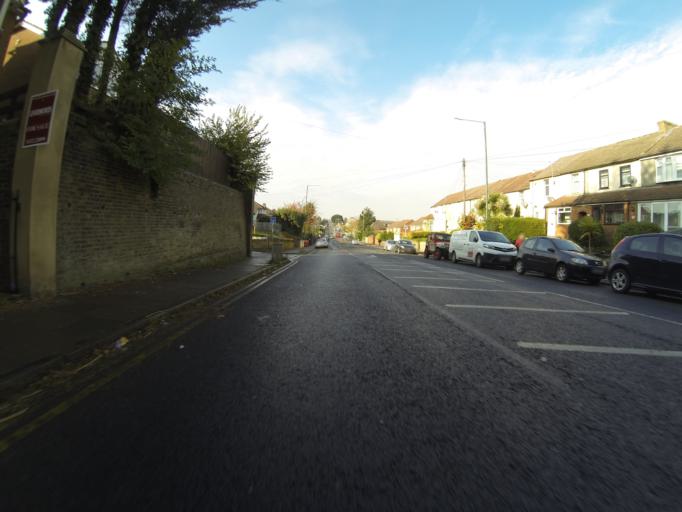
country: GB
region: England
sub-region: Kent
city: Dartford
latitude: 51.4478
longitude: 0.1964
